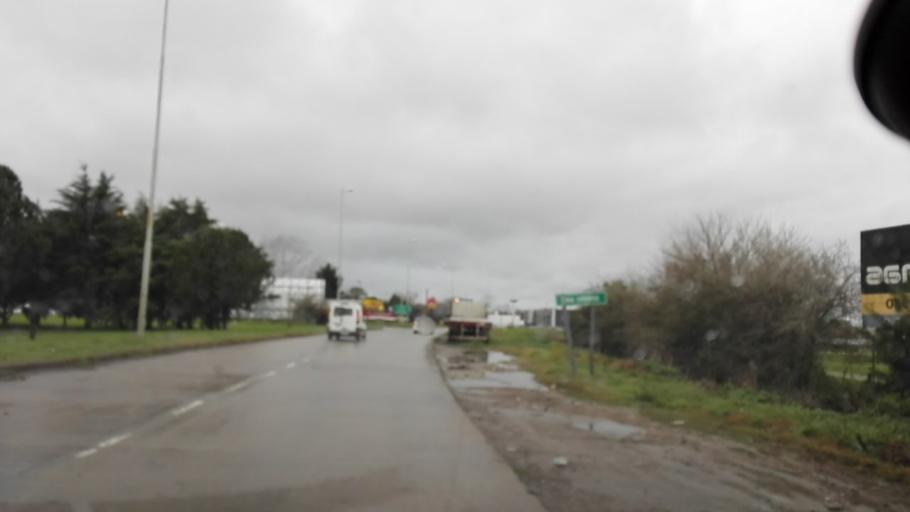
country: AR
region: Buenos Aires
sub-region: Partido de Brandsen
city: Brandsen
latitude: -35.1743
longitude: -58.2414
